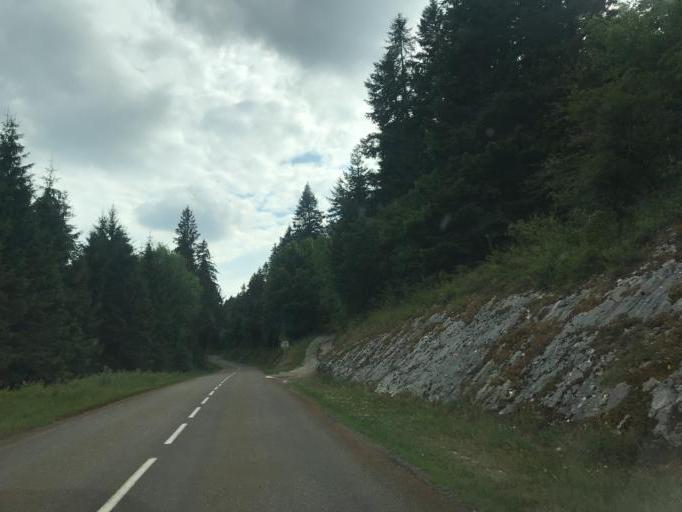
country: FR
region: Franche-Comte
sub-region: Departement du Jura
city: Valfin-les-Saint-Claude
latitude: 46.4946
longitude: 5.8501
